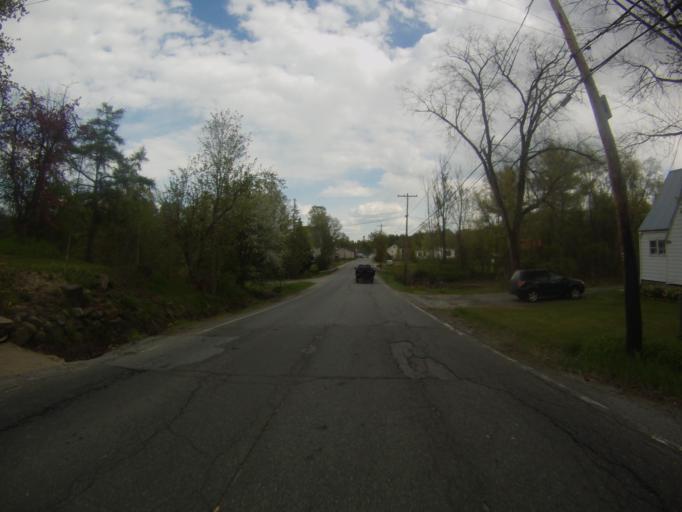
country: US
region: New York
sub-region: Essex County
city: Mineville
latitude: 44.0639
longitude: -73.5131
